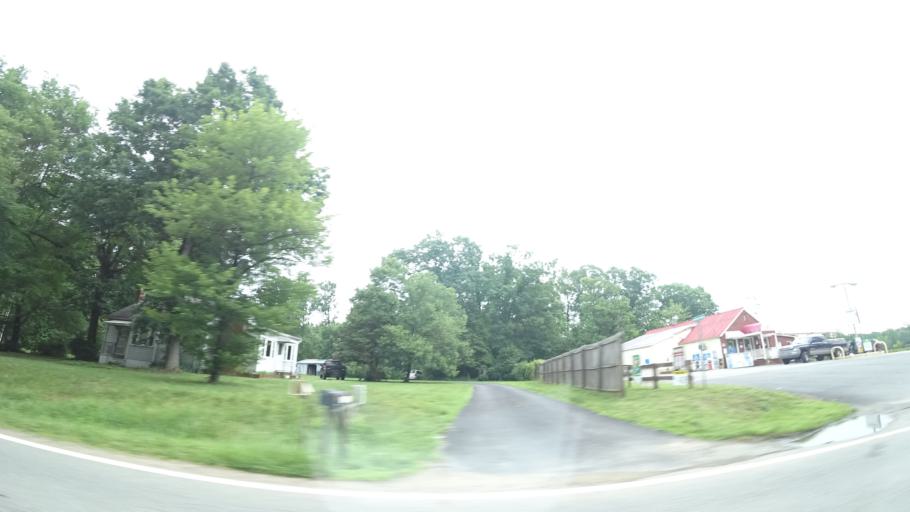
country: US
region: Virginia
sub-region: Spotsylvania County
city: Spotsylvania
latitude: 38.1305
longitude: -77.7836
